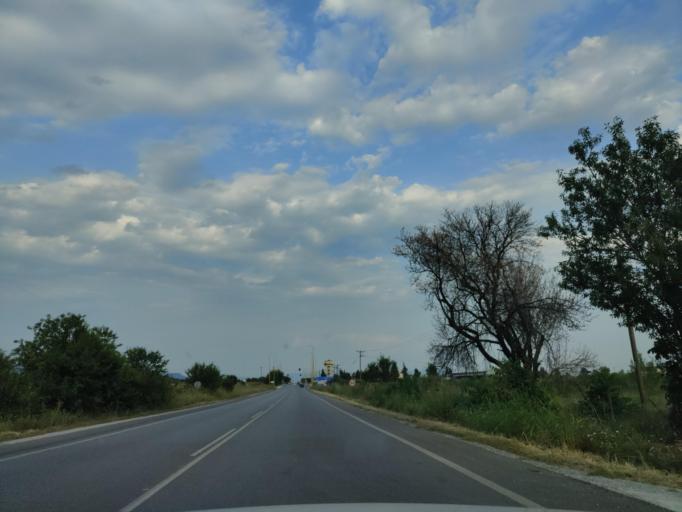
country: GR
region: East Macedonia and Thrace
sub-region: Nomos Dramas
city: Xiropotamos
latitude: 41.1642
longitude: 24.0674
